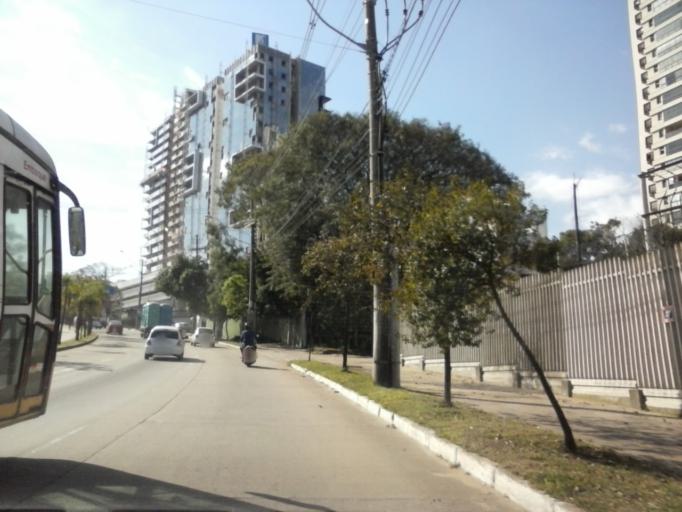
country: BR
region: Rio Grande do Sul
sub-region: Porto Alegre
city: Porto Alegre
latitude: -30.0423
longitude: -51.1733
